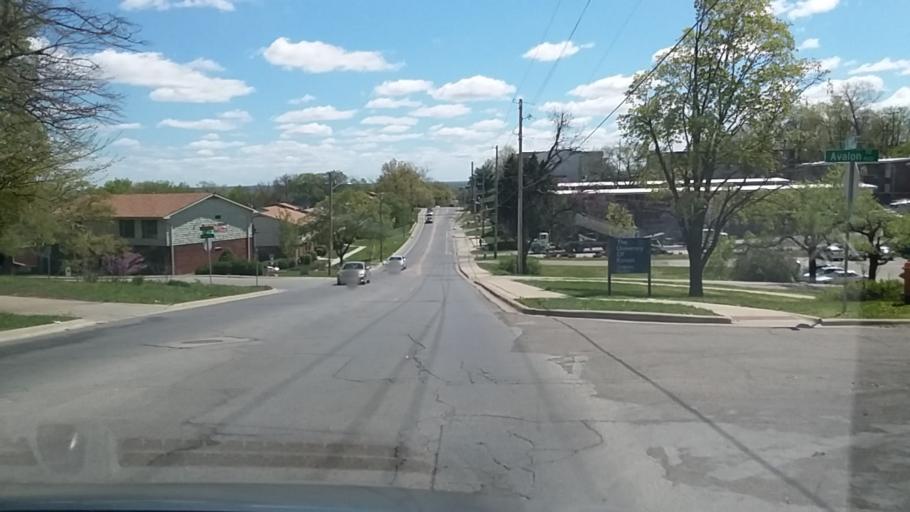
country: US
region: Kansas
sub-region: Douglas County
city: Lawrence
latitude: 38.9675
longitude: -95.2555
